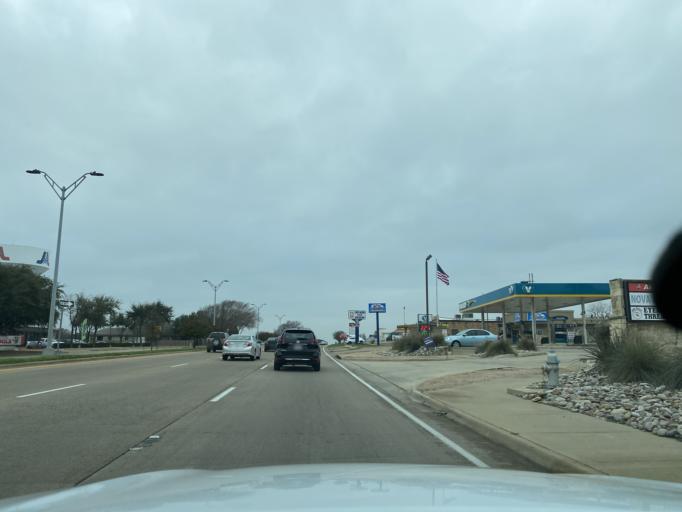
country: US
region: Texas
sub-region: Tarrant County
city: Arlington
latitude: 32.7082
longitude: -97.0904
